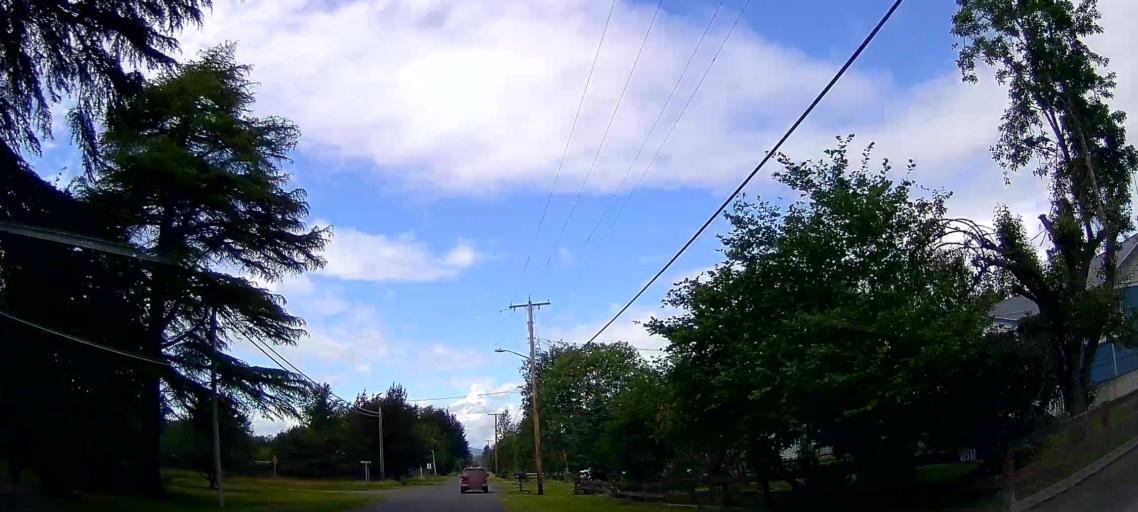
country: US
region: Washington
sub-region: Skagit County
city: Sedro-Woolley
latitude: 48.4912
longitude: -122.2373
